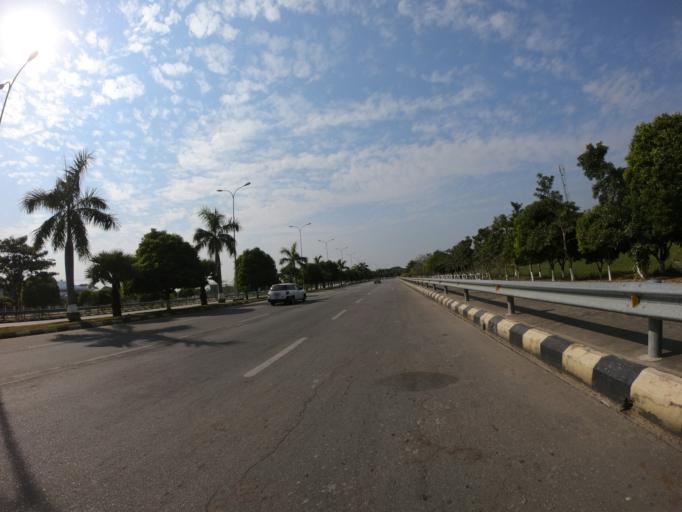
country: MM
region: Mandalay
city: Nay Pyi Taw
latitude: 19.6628
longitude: 96.1228
